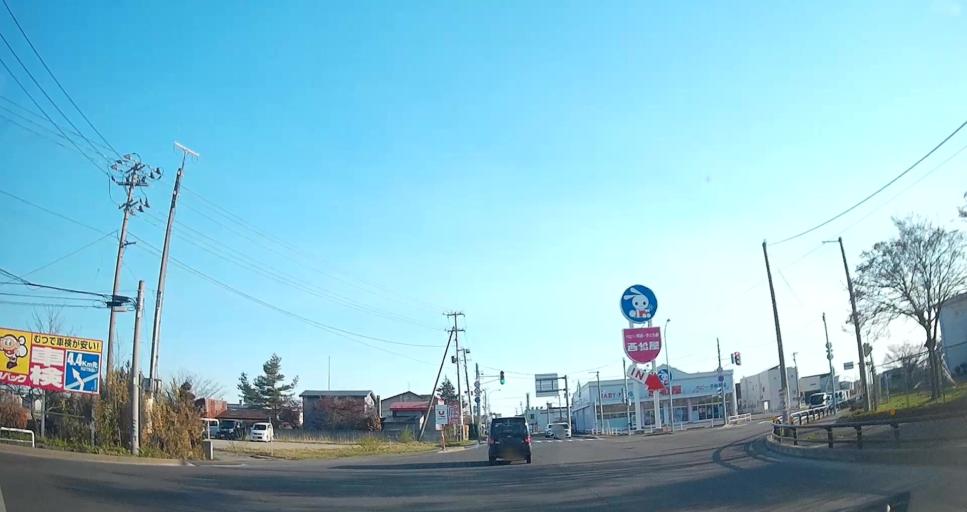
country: JP
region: Aomori
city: Mutsu
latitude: 41.2839
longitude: 141.2108
